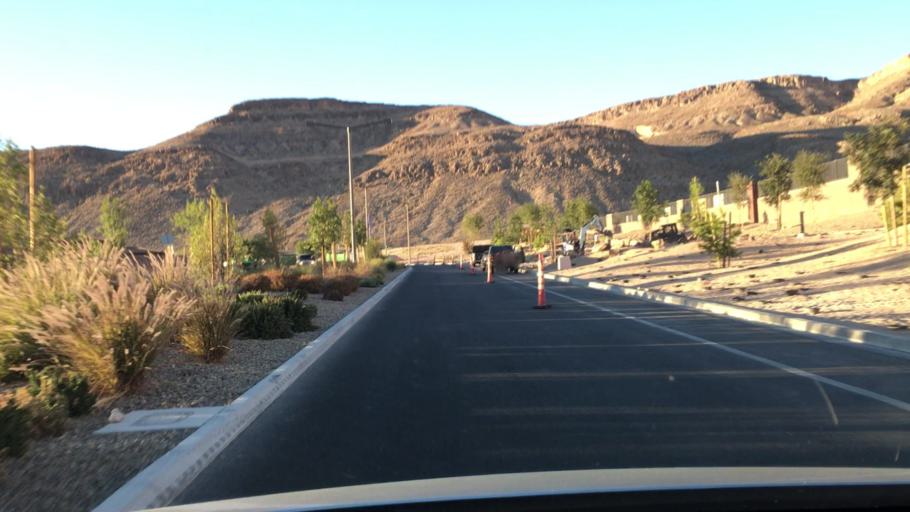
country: US
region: Nevada
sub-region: Clark County
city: Summerlin South
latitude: 36.0649
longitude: -115.3158
